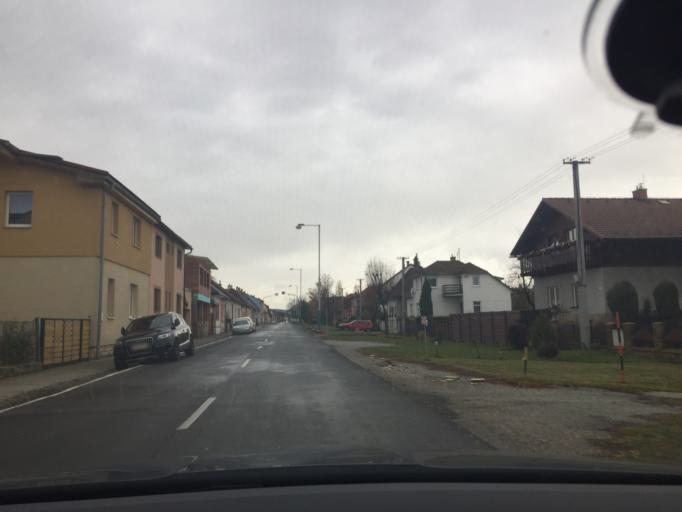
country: SK
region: Presovsky
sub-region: Okres Poprad
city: Poprad
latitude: 49.0628
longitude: 20.2836
